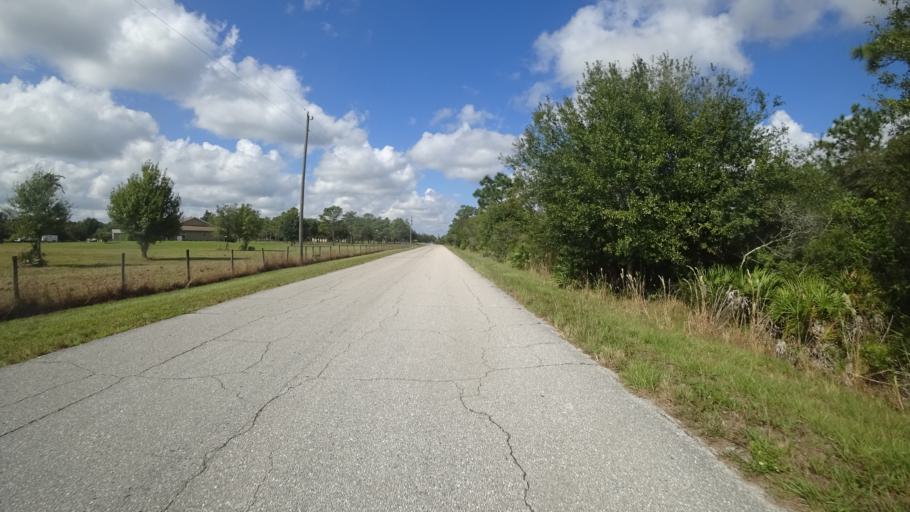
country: US
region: Florida
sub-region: Sarasota County
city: Fruitville
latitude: 27.4051
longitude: -82.2739
